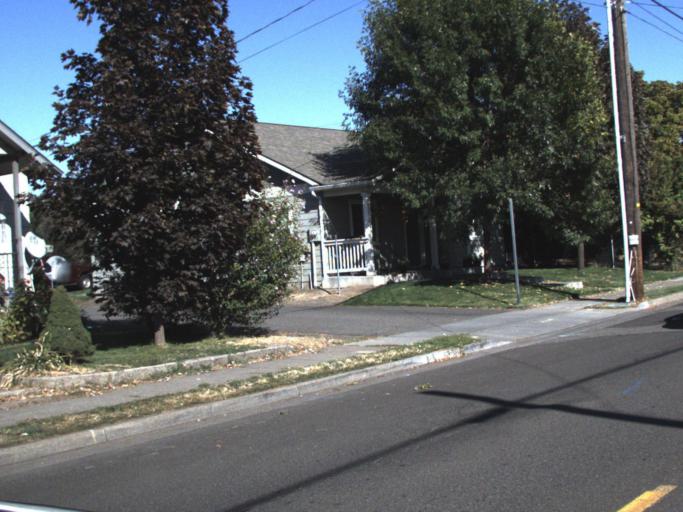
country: US
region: Washington
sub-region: Walla Walla County
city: College Place
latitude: 46.0014
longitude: -118.3875
